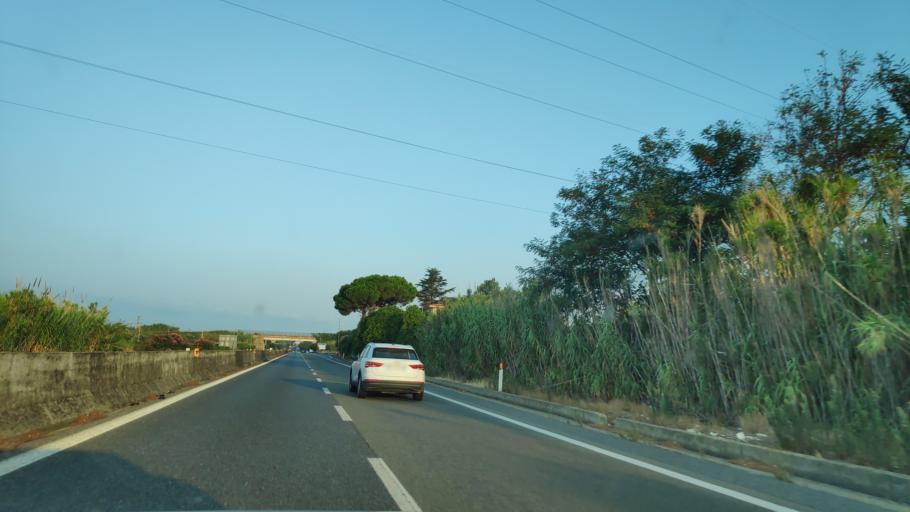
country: IT
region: Calabria
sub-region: Provincia di Catanzaro
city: Santa Eufemia Lamezia
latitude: 38.9133
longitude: 16.2952
